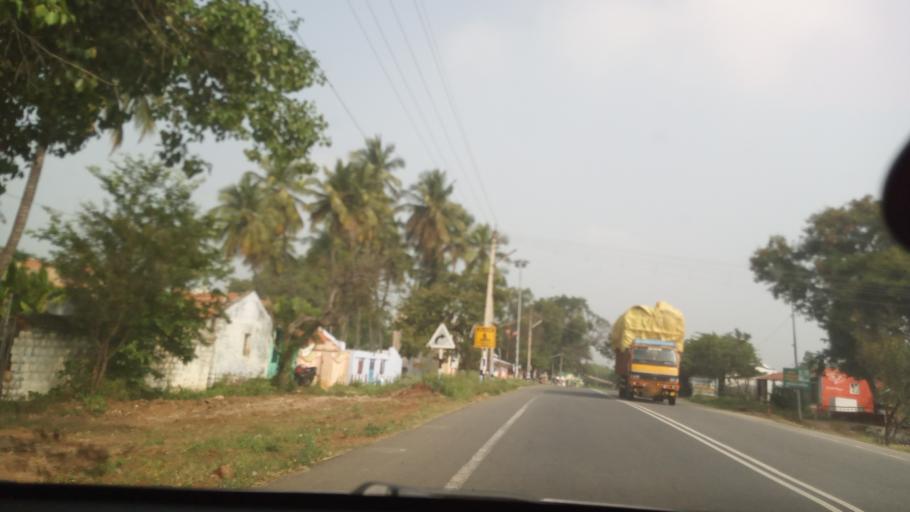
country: IN
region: Tamil Nadu
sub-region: Erode
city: Punjai Puliyampatti
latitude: 11.3813
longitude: 77.1725
